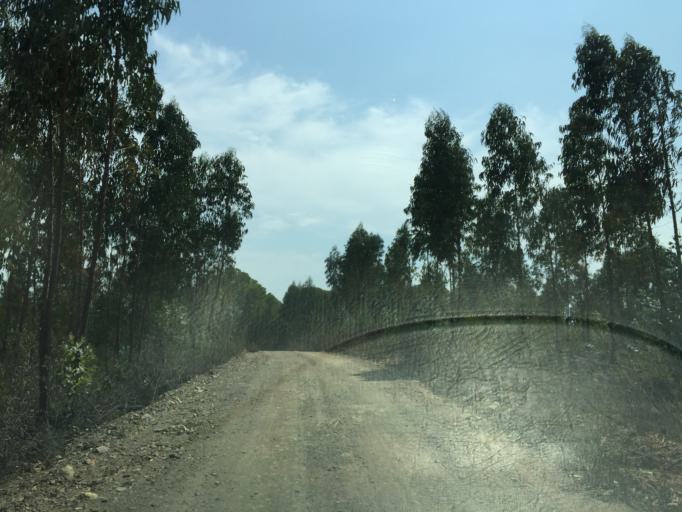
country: PT
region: Setubal
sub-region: Grandola
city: Grandola
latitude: 38.1084
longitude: -8.4915
